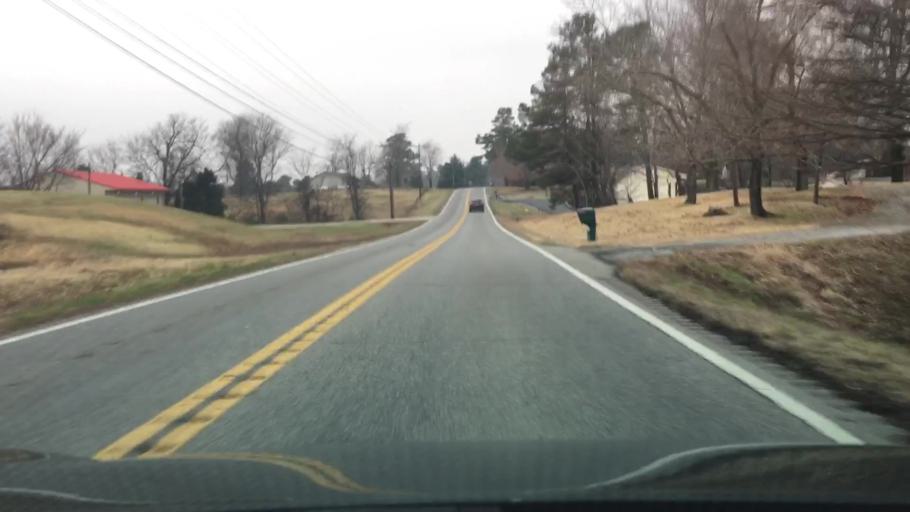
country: US
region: Kentucky
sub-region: Livingston County
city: Ledbetter
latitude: 36.9669
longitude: -88.4483
